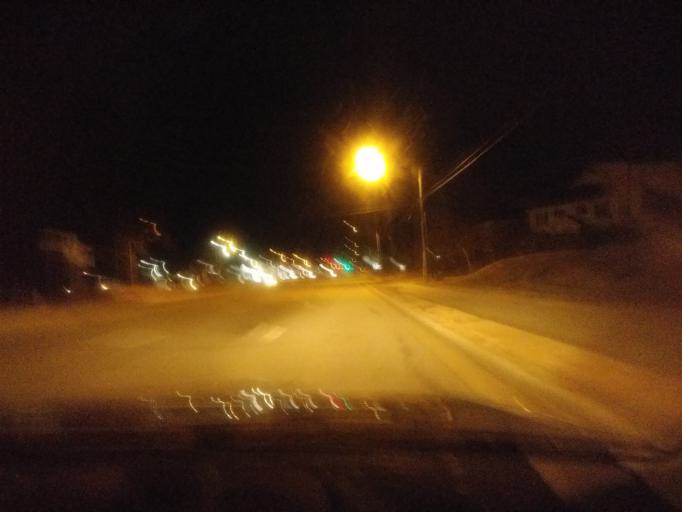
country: US
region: Virginia
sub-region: City of Chesapeake
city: Chesapeake
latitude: 36.7670
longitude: -76.2041
